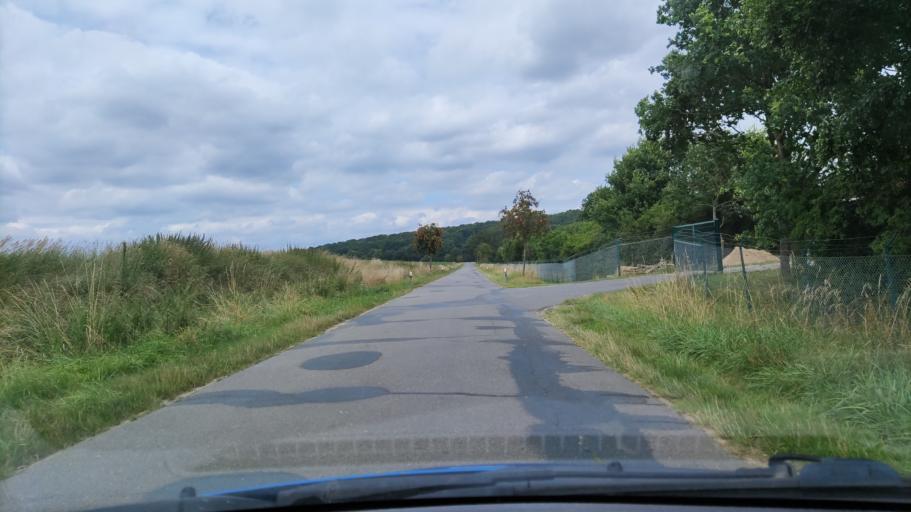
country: DE
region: Lower Saxony
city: Weste
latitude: 53.0746
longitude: 10.6895
